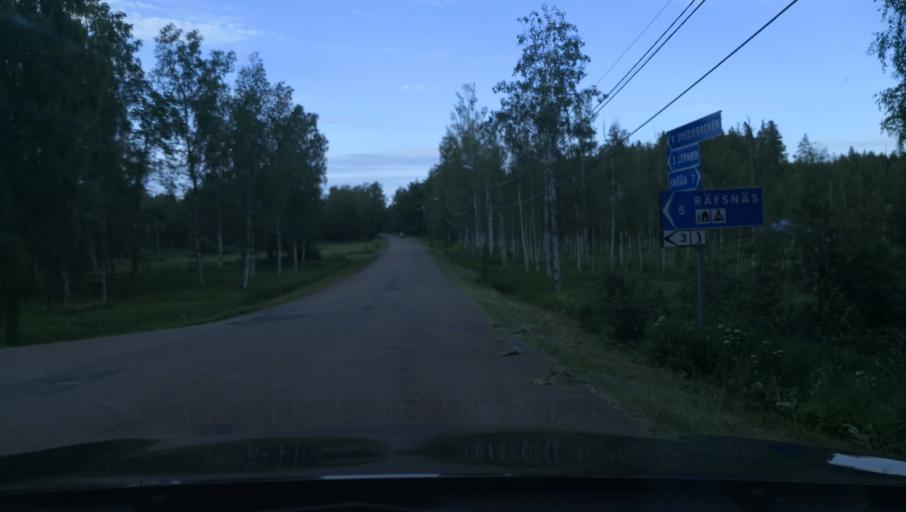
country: SE
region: Dalarna
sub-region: Ludvika Kommun
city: Ludvika
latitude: 60.1218
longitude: 15.2772
